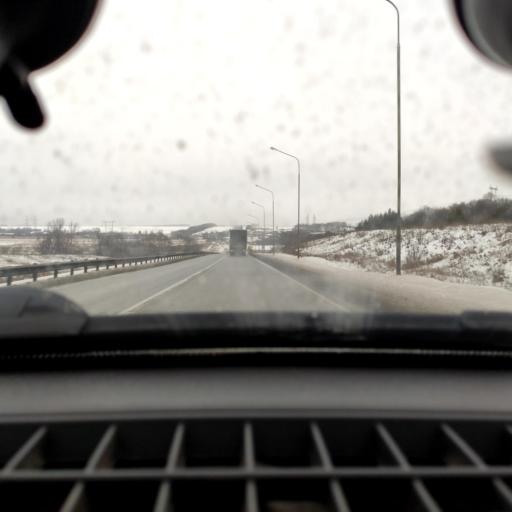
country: RU
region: Bashkortostan
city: Iglino
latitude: 54.7636
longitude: 56.4078
